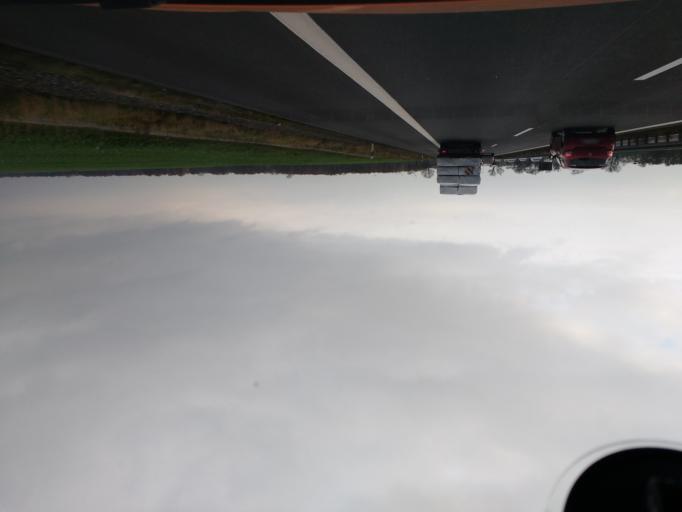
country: DE
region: Brandenburg
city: Dabergotz
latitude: 52.8755
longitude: 12.7592
